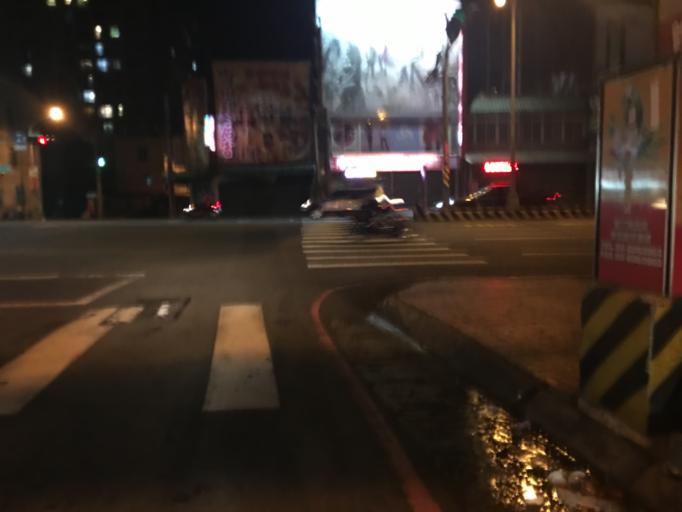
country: TW
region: Taiwan
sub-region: Hsinchu
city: Zhubei
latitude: 24.8288
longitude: 120.9998
